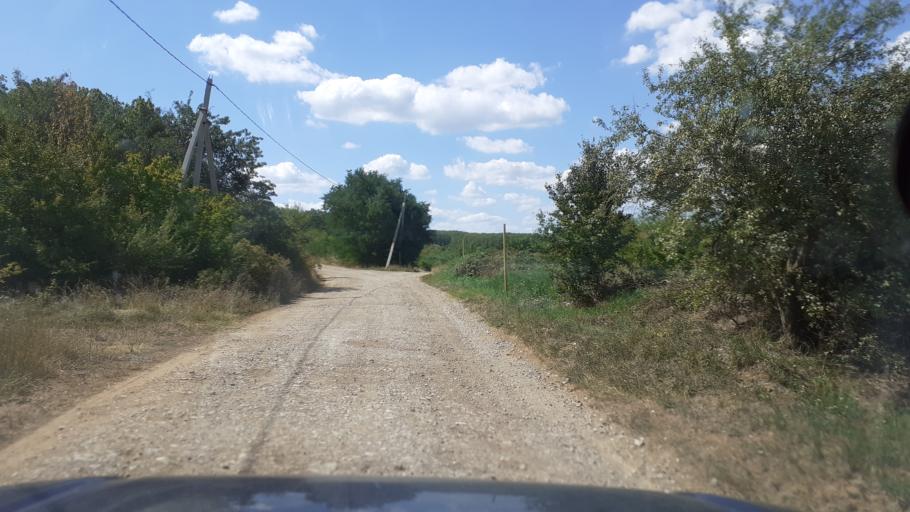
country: RU
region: Krasnodarskiy
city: Il'skiy
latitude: 44.8243
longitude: 38.5922
